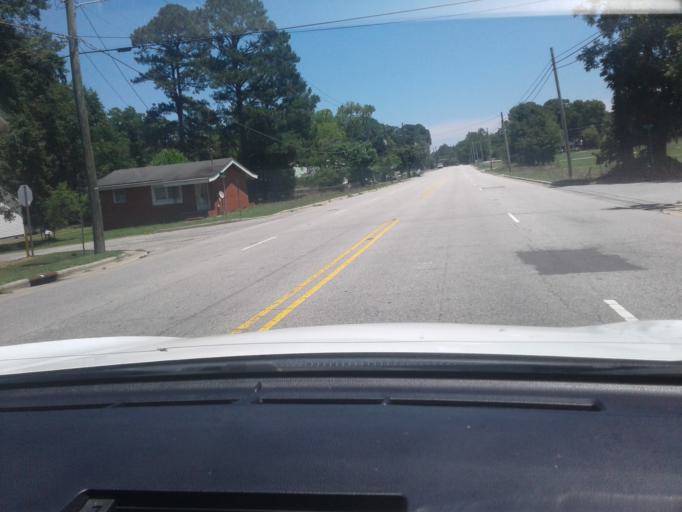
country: US
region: North Carolina
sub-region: Harnett County
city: Lillington
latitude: 35.3933
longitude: -78.8173
